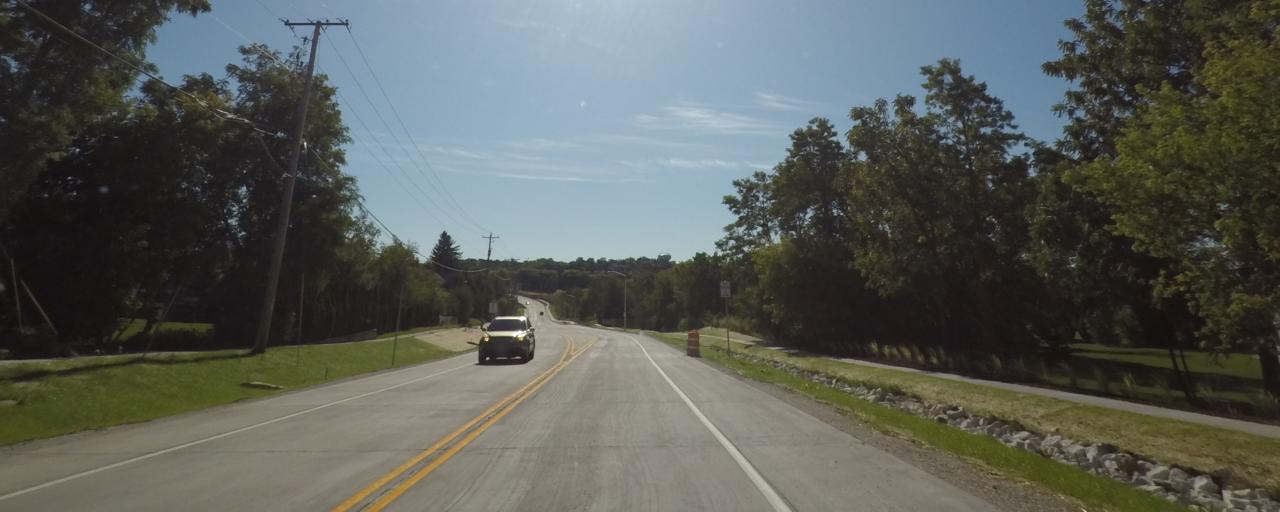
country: US
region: Wisconsin
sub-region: Waukesha County
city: Pewaukee
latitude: 43.0345
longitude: -88.2812
